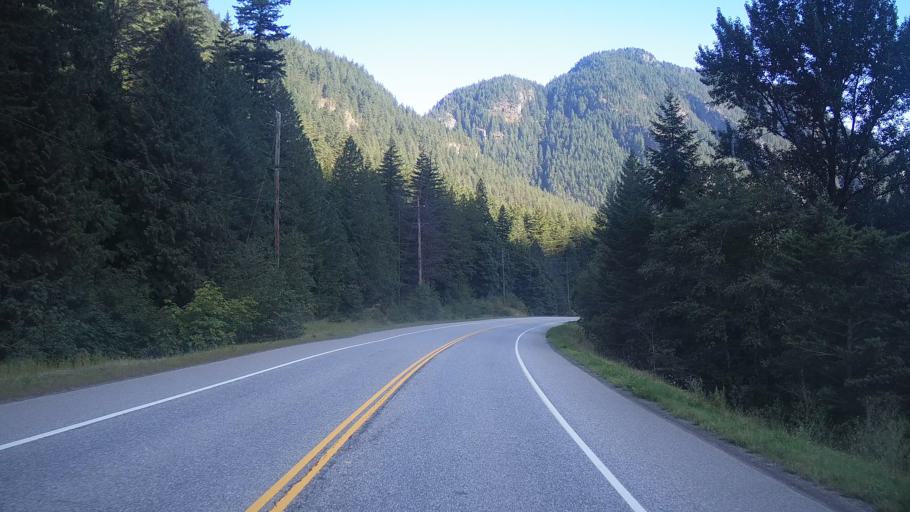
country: CA
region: British Columbia
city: Hope
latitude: 49.6004
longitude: -121.4157
